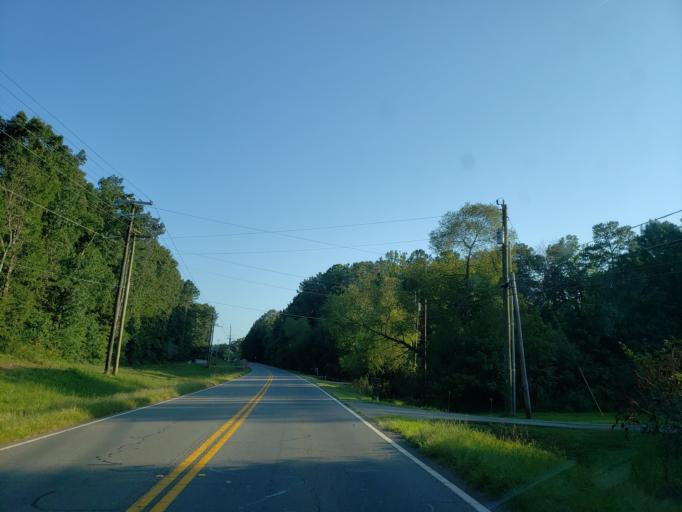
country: US
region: Georgia
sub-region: Murray County
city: Chatsworth
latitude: 34.7358
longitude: -84.8204
